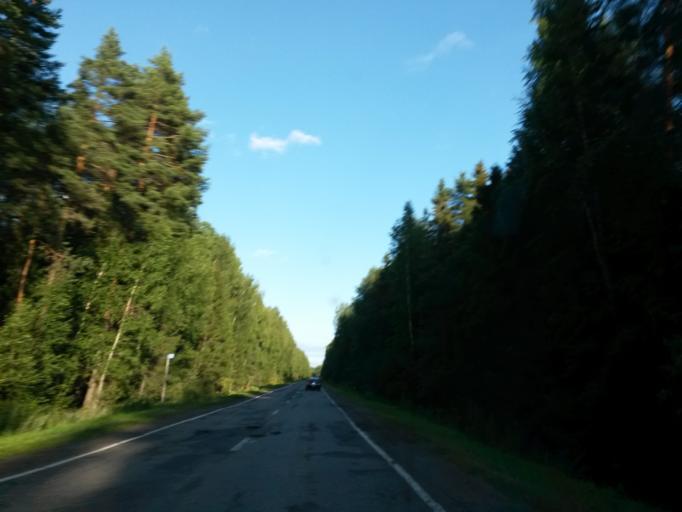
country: RU
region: Jaroslavl
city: Yaroslavl
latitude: 57.8037
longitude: 39.7840
